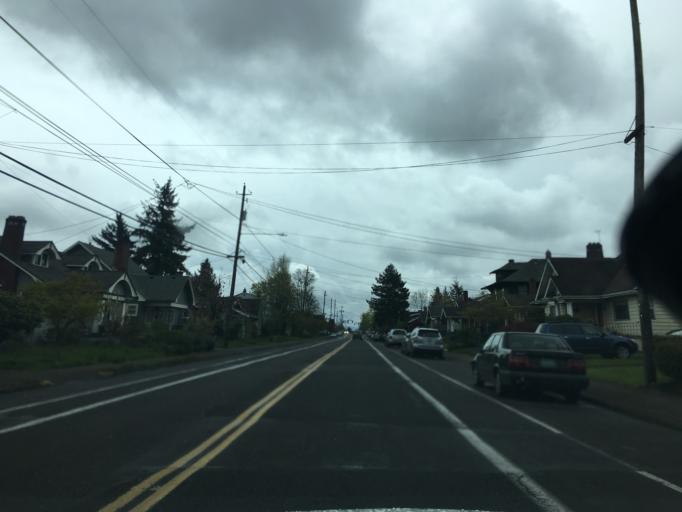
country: US
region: Oregon
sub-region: Multnomah County
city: Portland
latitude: 45.5453
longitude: -122.6046
